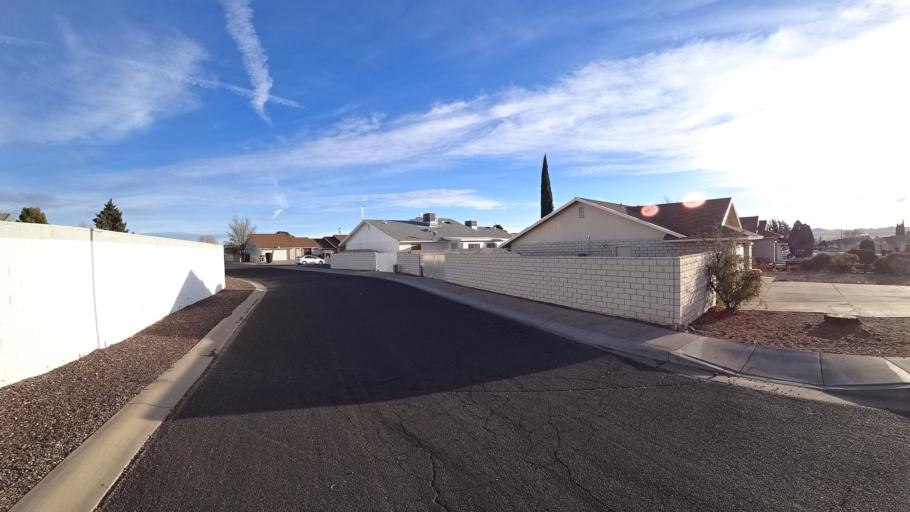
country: US
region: Arizona
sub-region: Mohave County
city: New Kingman-Butler
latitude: 35.2418
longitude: -114.0433
